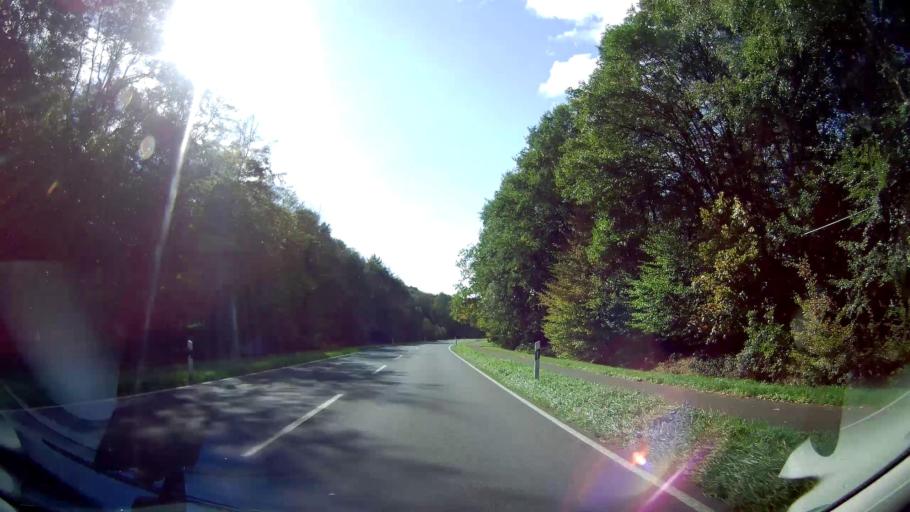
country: DE
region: North Rhine-Westphalia
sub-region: Regierungsbezirk Dusseldorf
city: Hunxe
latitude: 51.5998
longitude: 6.8234
